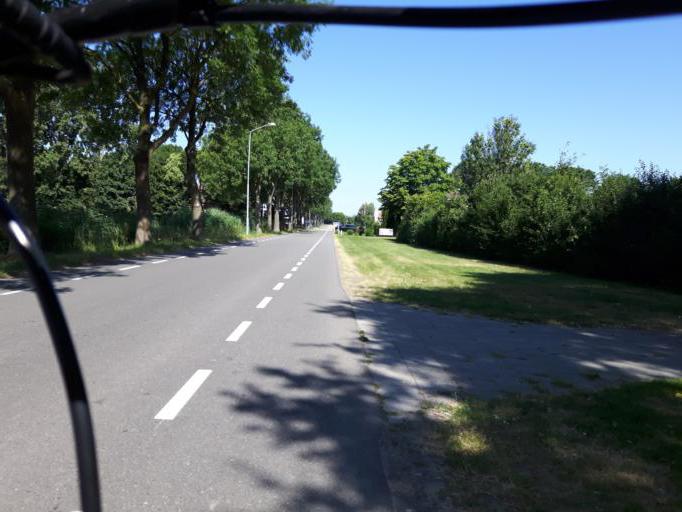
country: NL
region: North Brabant
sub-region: Gemeente Moerdijk
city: Klundert
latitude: 51.6710
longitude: 4.5304
